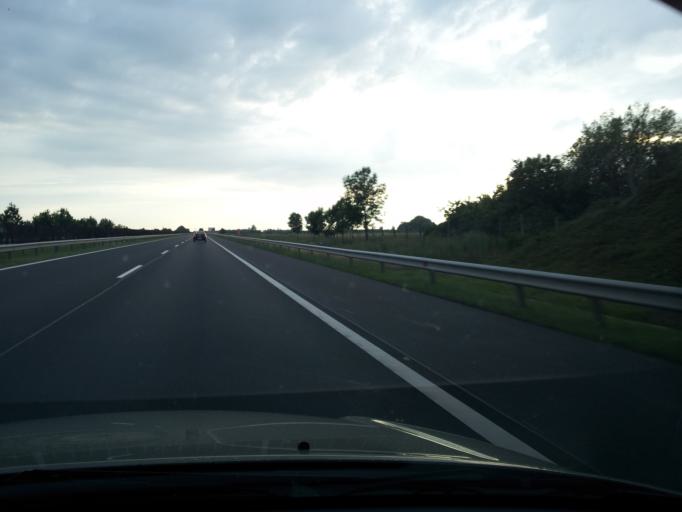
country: HU
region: Heves
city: Kompolt
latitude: 47.7097
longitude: 20.1878
